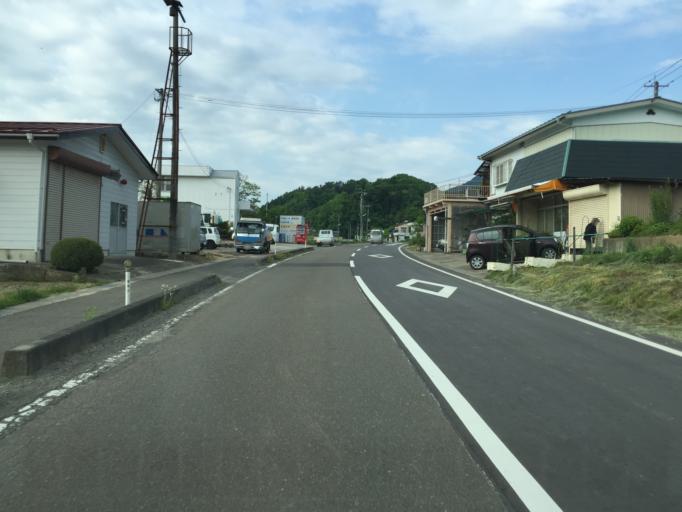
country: JP
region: Fukushima
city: Hobaramachi
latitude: 37.7257
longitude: 140.5974
